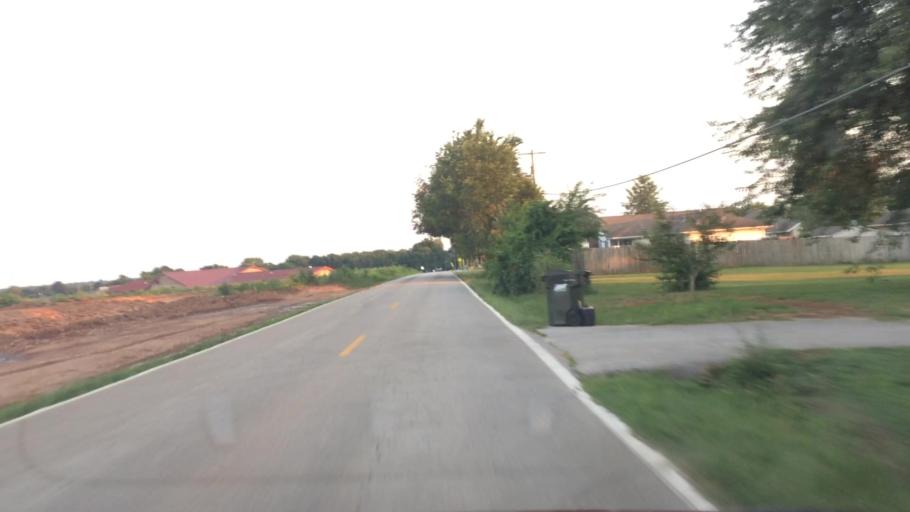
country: US
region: Missouri
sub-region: Greene County
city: Springfield
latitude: 37.2025
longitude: -93.3743
